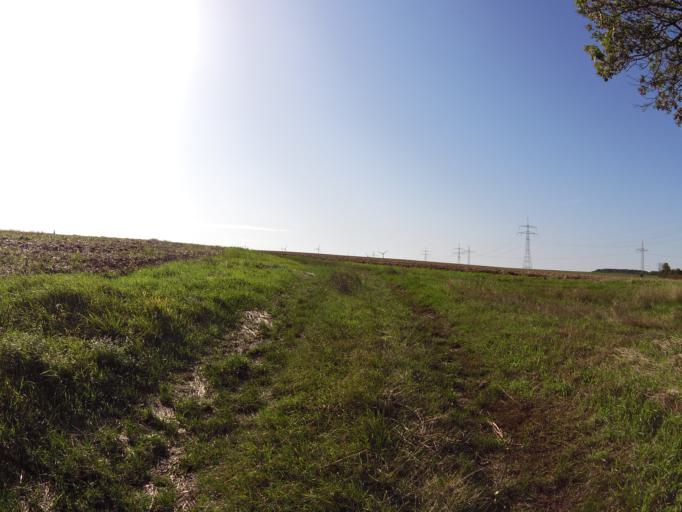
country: DE
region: Bavaria
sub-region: Regierungsbezirk Unterfranken
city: Theilheim
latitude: 49.7518
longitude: 10.0593
